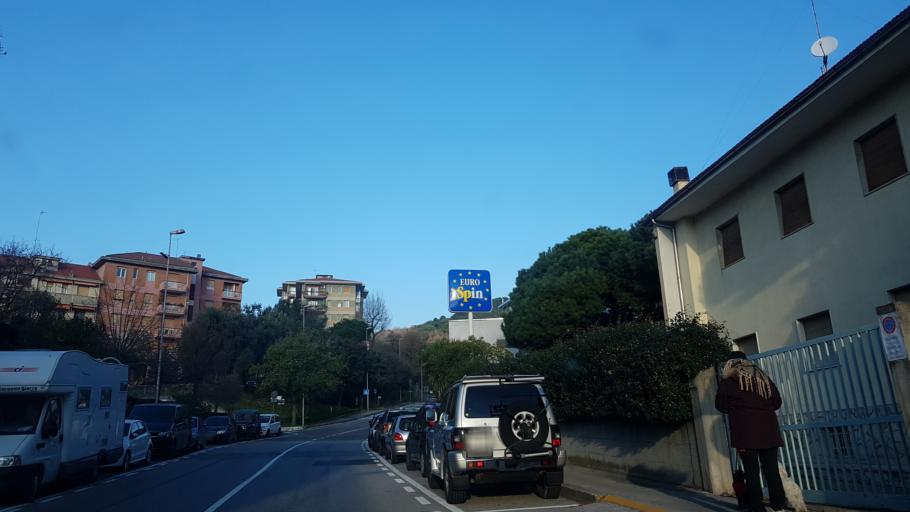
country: IT
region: Liguria
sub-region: Provincia di Savona
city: Savona
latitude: 44.3056
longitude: 8.4668
